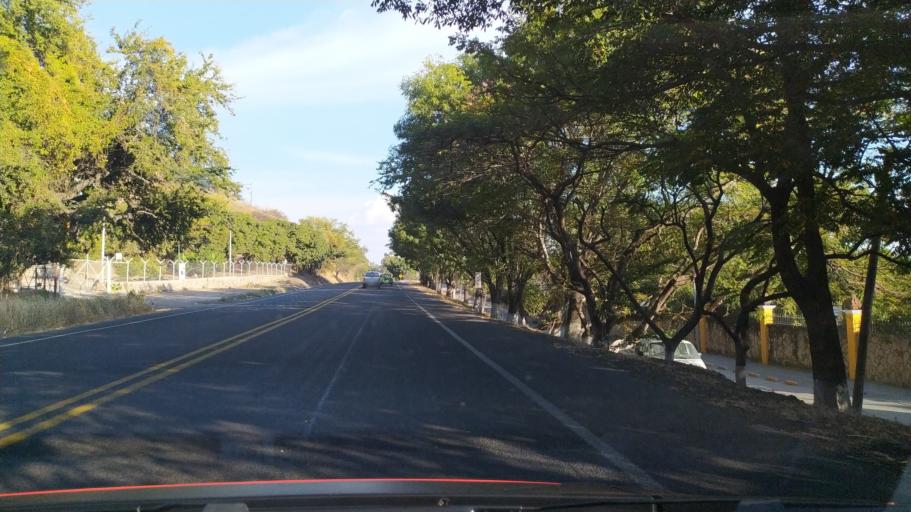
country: MX
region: Jalisco
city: Jamay
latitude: 20.2939
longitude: -102.7330
